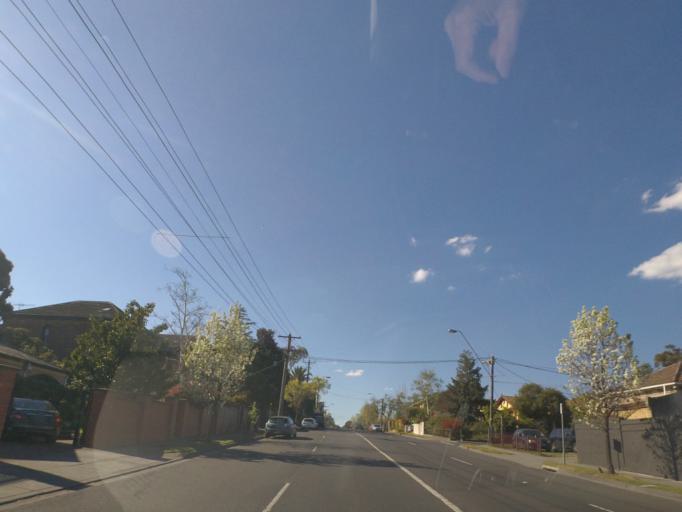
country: AU
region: Victoria
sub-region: Boroondara
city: Kew
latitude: -37.8164
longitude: 145.0273
